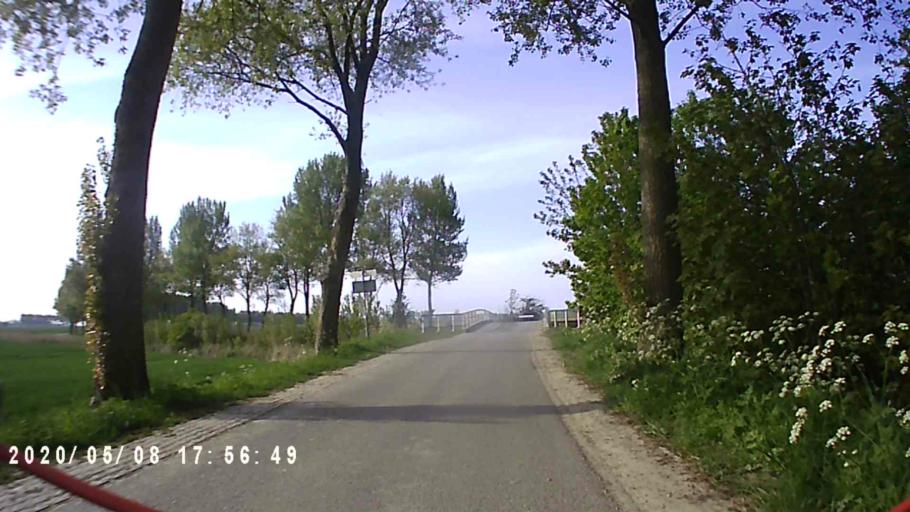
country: NL
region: Groningen
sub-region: Gemeente Winsum
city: Winsum
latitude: 53.3664
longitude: 6.4887
